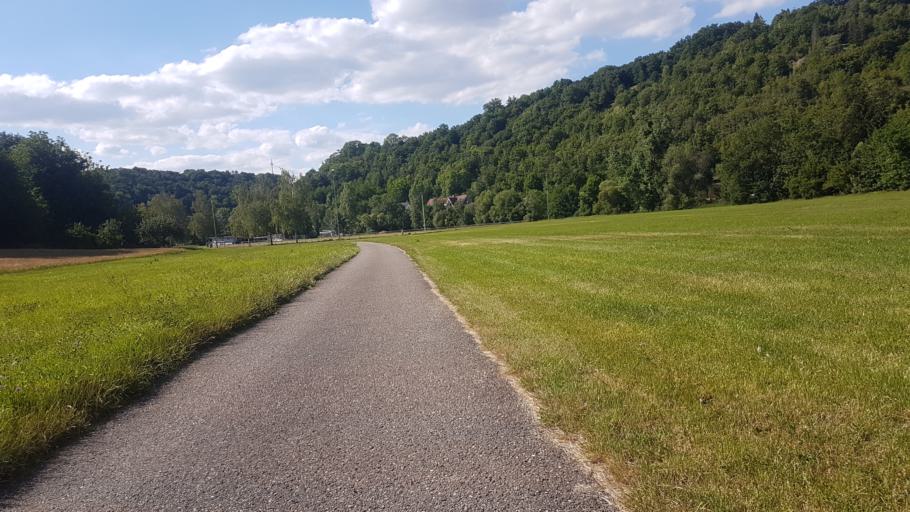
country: DE
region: Baden-Wuerttemberg
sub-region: Regierungsbezirk Stuttgart
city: Widdern
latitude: 49.3148
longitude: 9.4269
